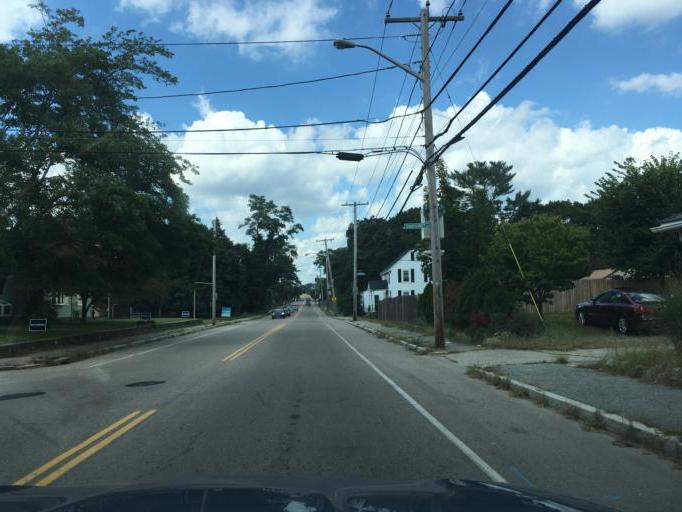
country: US
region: Rhode Island
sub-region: Kent County
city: Warwick
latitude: 41.6960
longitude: -71.3986
